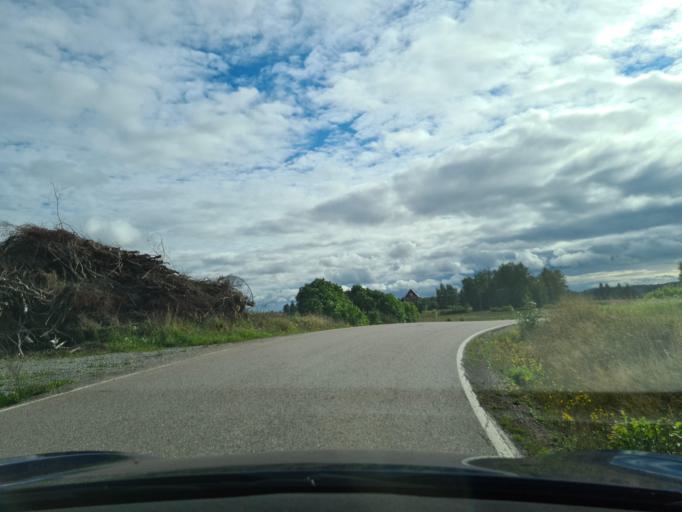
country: FI
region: Uusimaa
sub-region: Helsinki
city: Vihti
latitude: 60.4453
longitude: 24.3955
